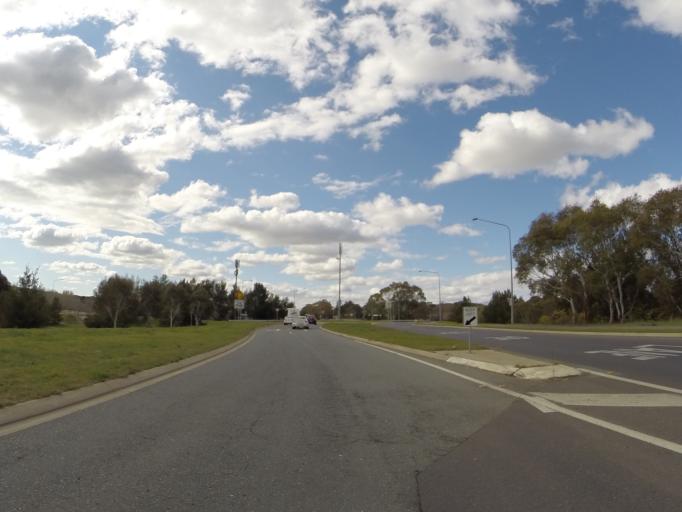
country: AU
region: Australian Capital Territory
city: Belconnen
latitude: -35.2144
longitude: 149.0863
